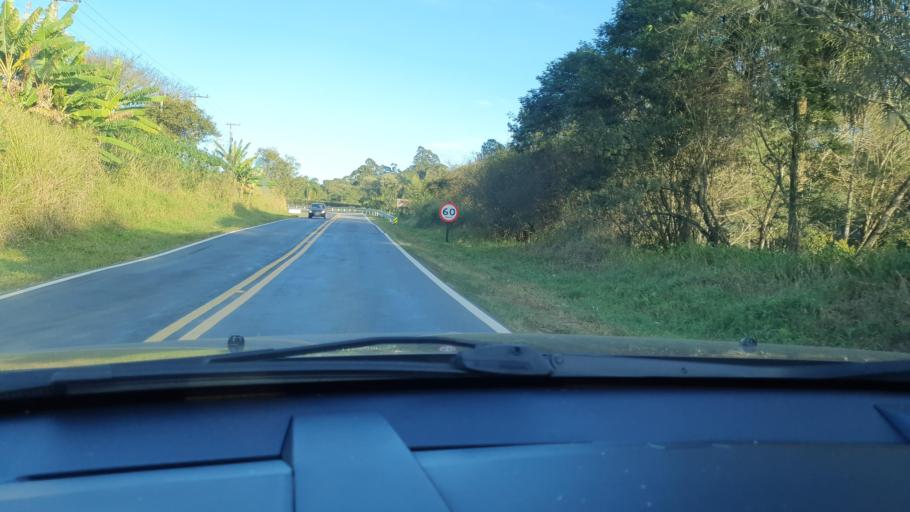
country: BR
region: Sao Paulo
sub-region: Ibiuna
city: Ibiuna
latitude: -23.6767
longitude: -47.3260
